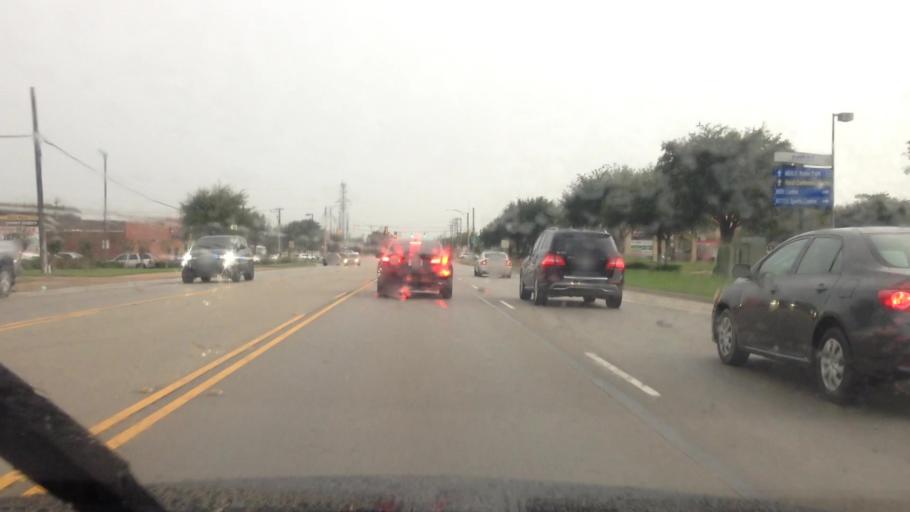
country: US
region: Texas
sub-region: Tarrant County
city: Hurst
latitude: 32.8543
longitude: -97.1880
